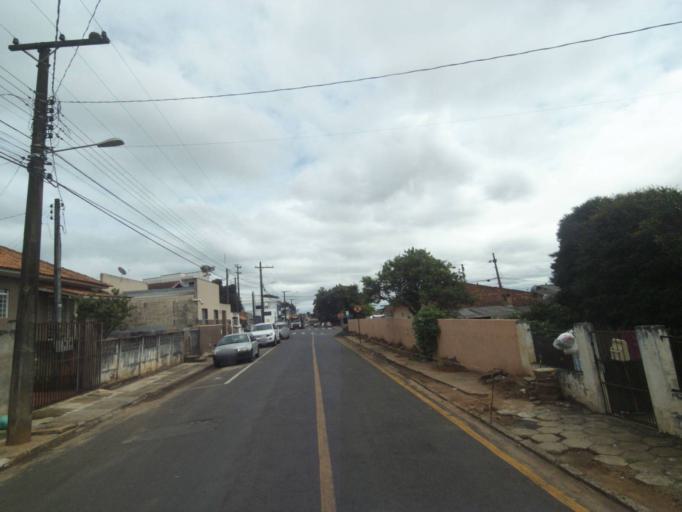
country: BR
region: Parana
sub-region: Telemaco Borba
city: Telemaco Borba
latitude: -24.3319
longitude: -50.6272
